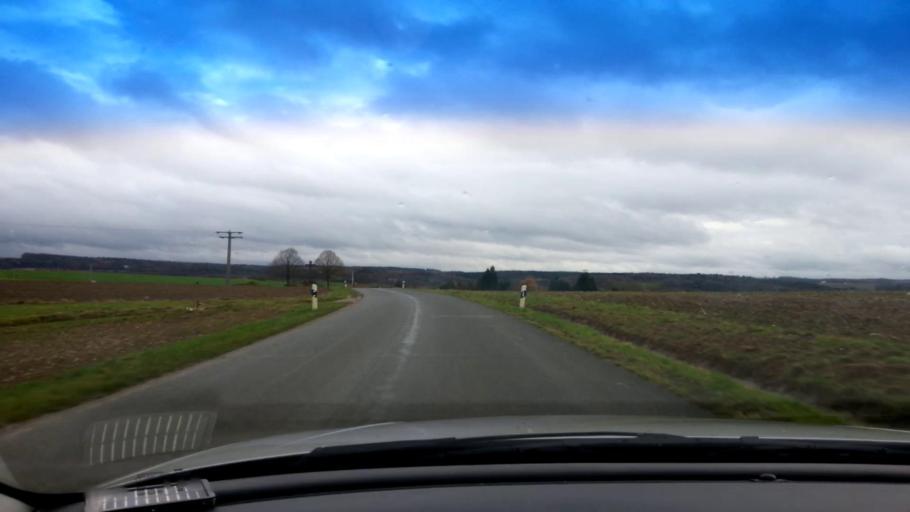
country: DE
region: Bavaria
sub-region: Upper Franconia
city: Zapfendorf
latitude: 50.0254
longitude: 10.9693
